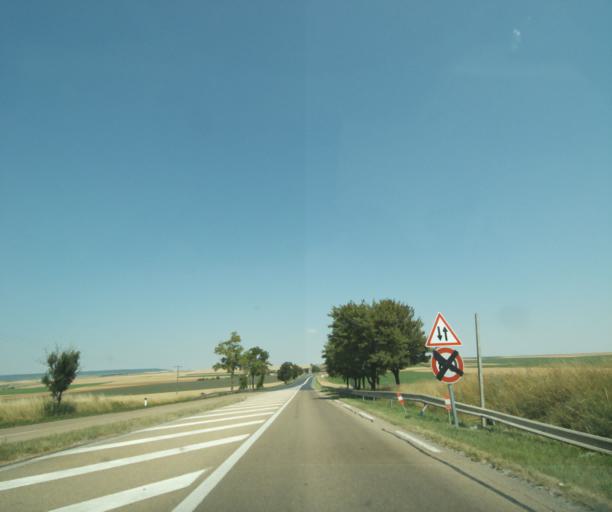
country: FR
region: Champagne-Ardenne
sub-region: Departement de la Marne
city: Fagnieres
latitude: 49.0556
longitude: 4.3003
